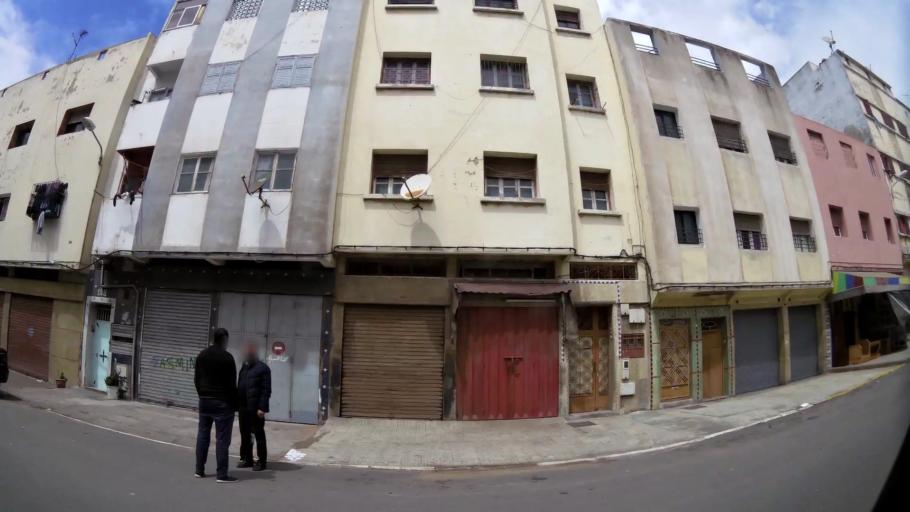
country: MA
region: Grand Casablanca
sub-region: Mediouna
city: Tit Mellil
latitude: 33.6050
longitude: -7.5170
